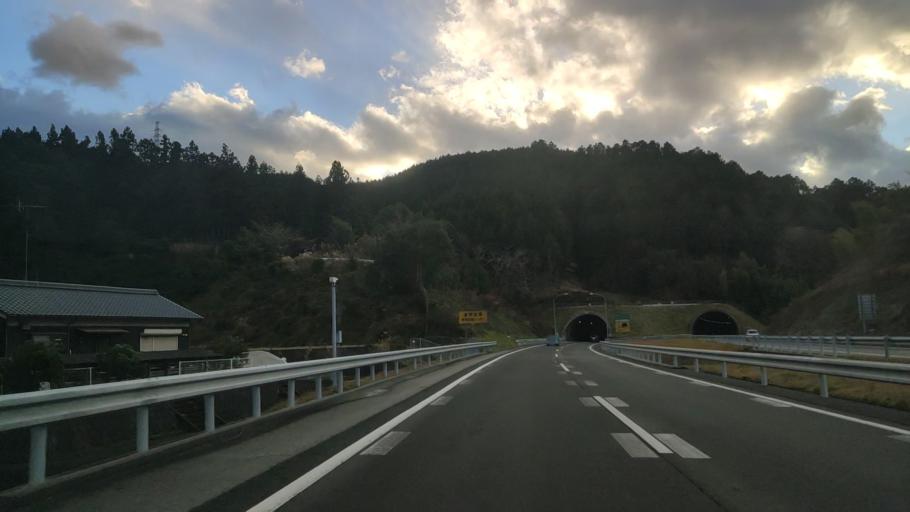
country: JP
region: Ehime
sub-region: Shikoku-chuo Shi
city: Matsuyama
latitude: 33.7923
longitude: 132.9256
